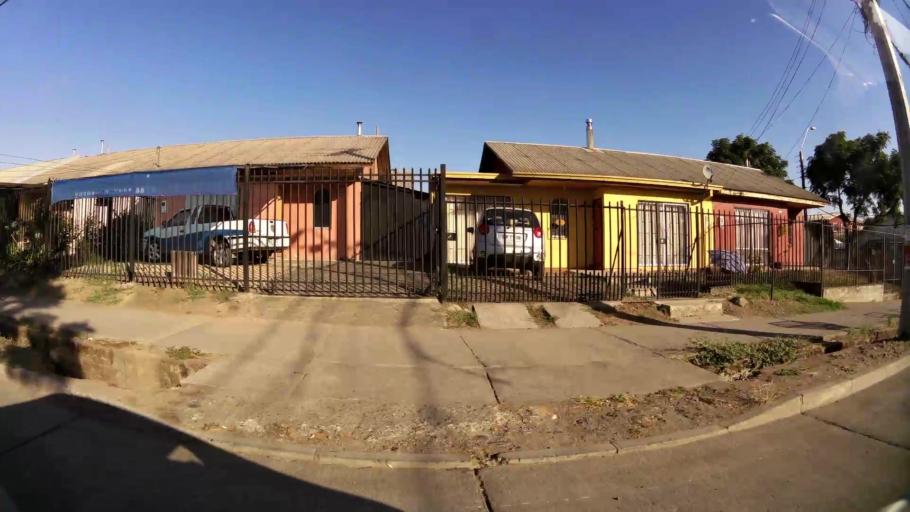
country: CL
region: Maule
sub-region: Provincia de Talca
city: Talca
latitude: -35.4383
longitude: -71.6915
